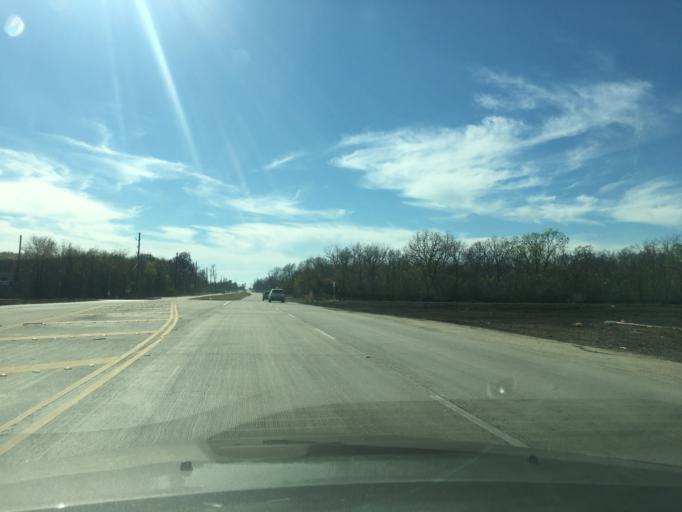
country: US
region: Texas
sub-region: Fort Bend County
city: Greatwood
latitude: 29.5550
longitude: -95.7176
